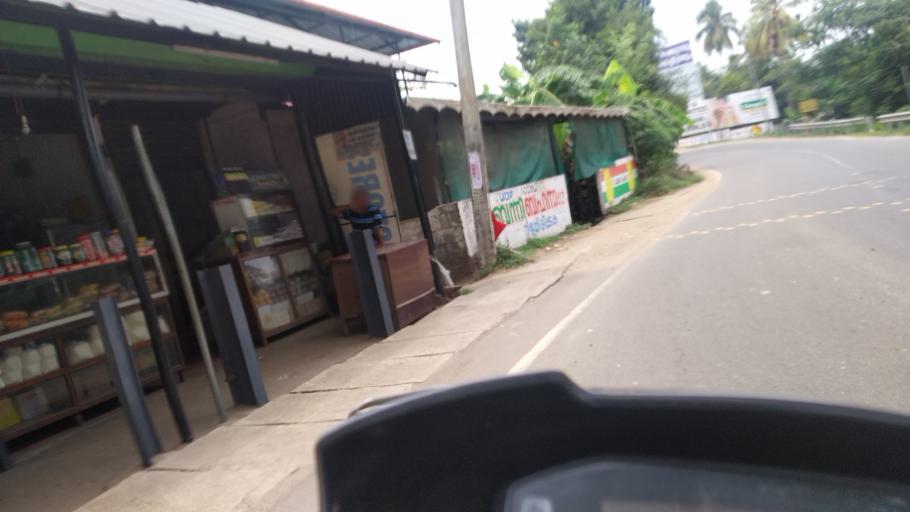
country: IN
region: Kerala
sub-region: Ernakulam
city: Aluva
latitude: 10.1567
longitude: 76.3269
